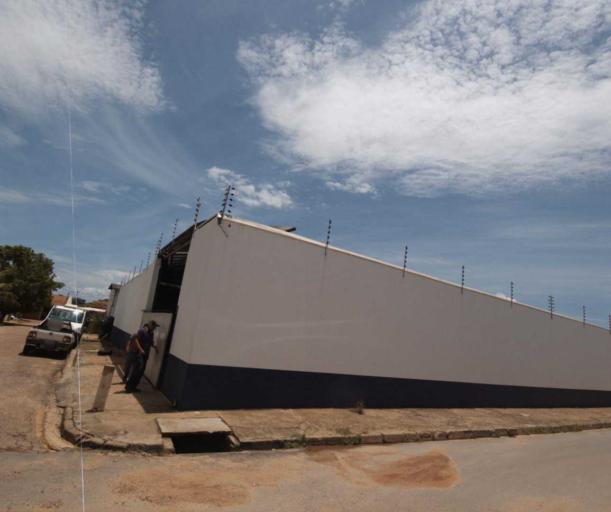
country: BR
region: Mato Grosso
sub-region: Varzea Grande
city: Varzea Grande
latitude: -15.6247
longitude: -56.1152
